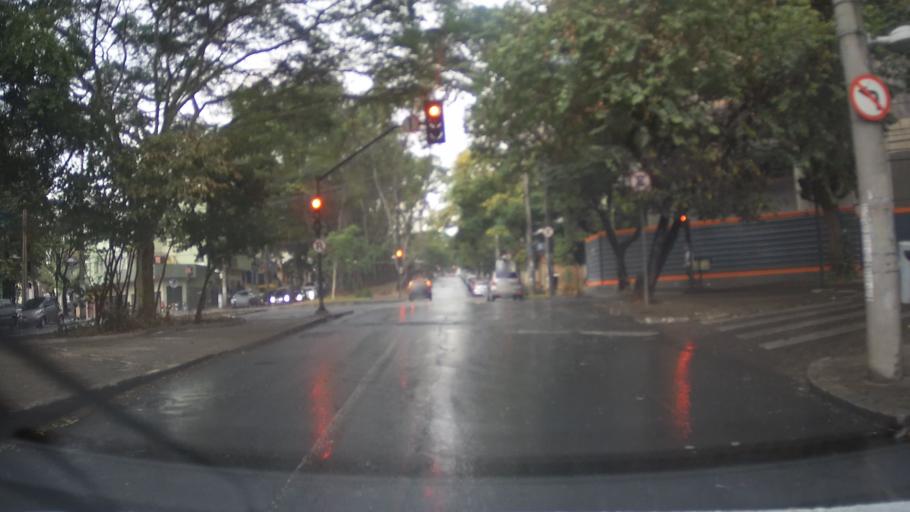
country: BR
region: Minas Gerais
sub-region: Belo Horizonte
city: Belo Horizonte
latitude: -19.9213
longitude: -43.9550
